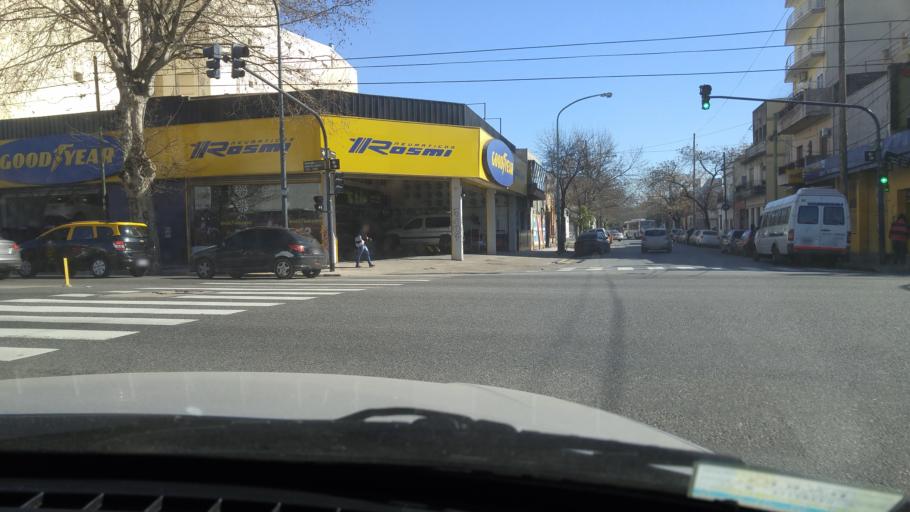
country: AR
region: Buenos Aires F.D.
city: Colegiales
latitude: -34.5980
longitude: -58.4486
